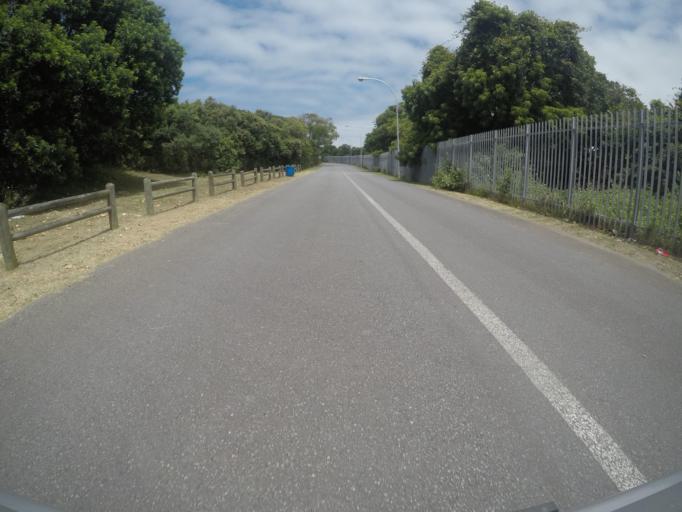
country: ZA
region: Eastern Cape
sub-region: Buffalo City Metropolitan Municipality
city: East London
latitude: -33.0229
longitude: 27.9102
